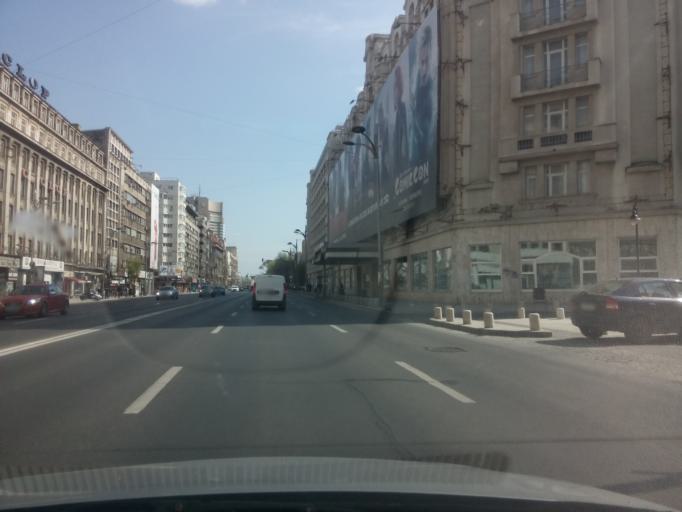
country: RO
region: Bucuresti
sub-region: Municipiul Bucuresti
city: Bucharest
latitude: 44.4421
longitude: 26.0990
